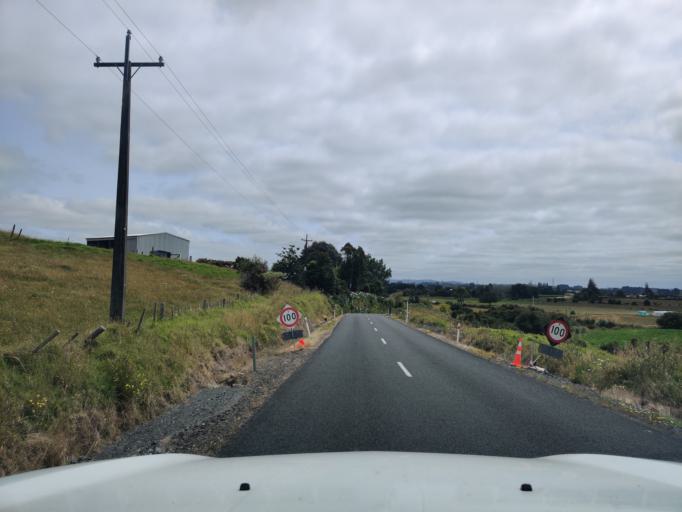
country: NZ
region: Waikato
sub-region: Waikato District
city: Te Kauwhata
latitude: -37.5254
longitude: 175.1720
